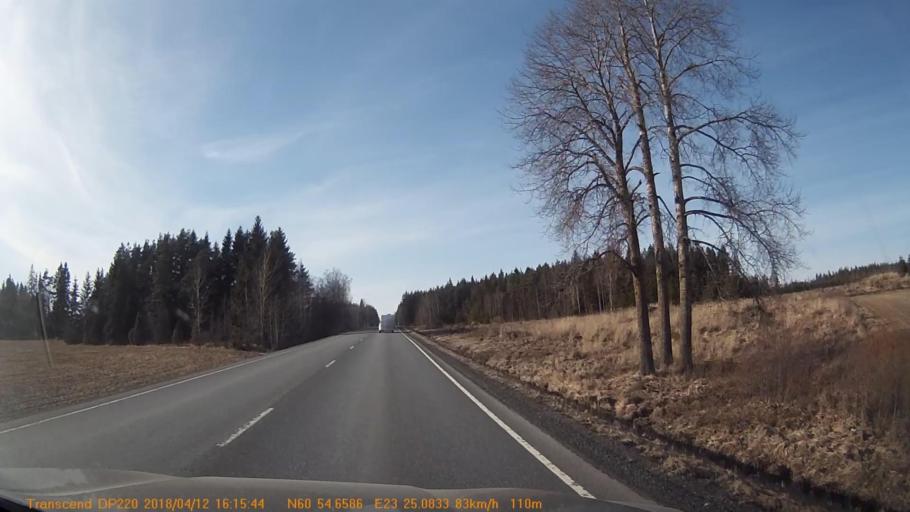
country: FI
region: Haeme
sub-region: Forssa
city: Humppila
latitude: 60.9111
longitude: 23.4178
